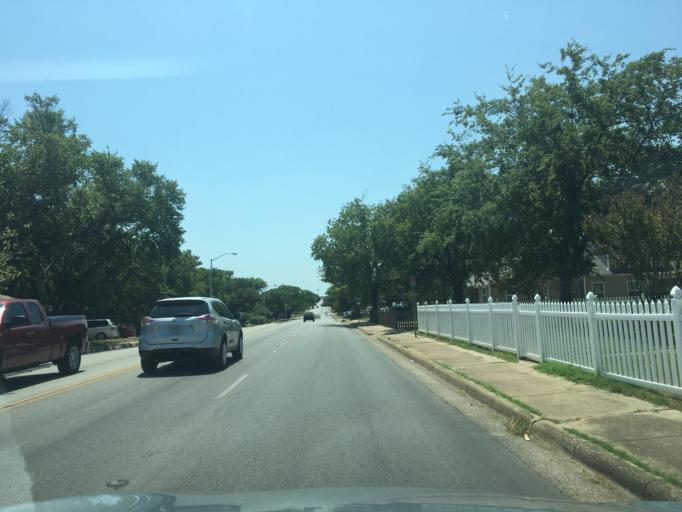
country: US
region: Texas
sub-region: Tarrant County
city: Edgecliff Village
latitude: 32.6818
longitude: -97.3531
